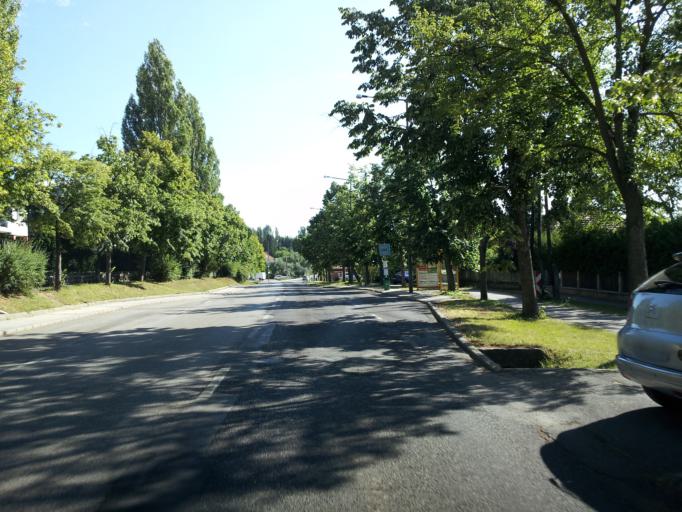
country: HU
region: Veszprem
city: Veszprem
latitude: 47.0857
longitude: 17.8994
